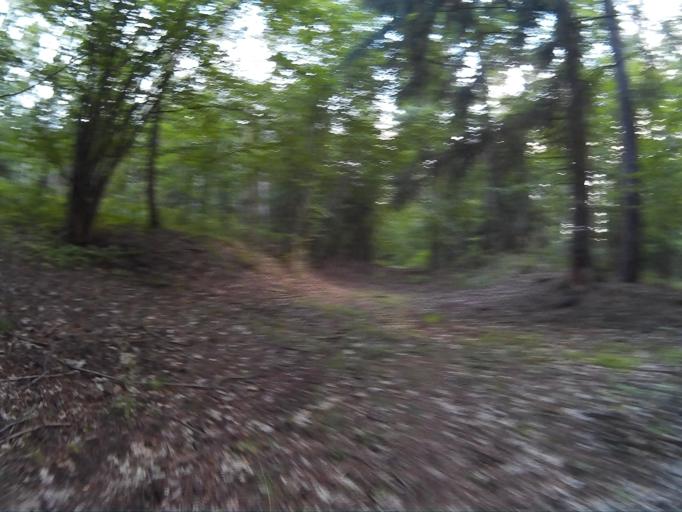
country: PL
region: Kujawsko-Pomorskie
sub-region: Powiat swiecki
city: Lniano
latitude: 53.5503
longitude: 18.1259
